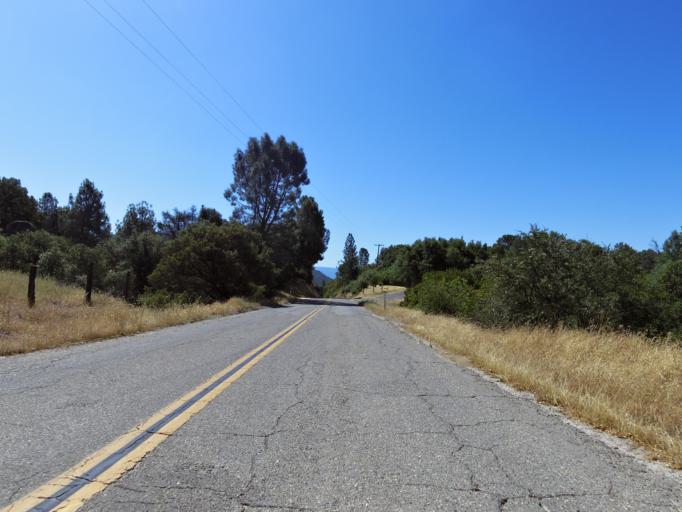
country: US
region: California
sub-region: Fresno County
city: Auberry
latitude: 37.2082
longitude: -119.4776
